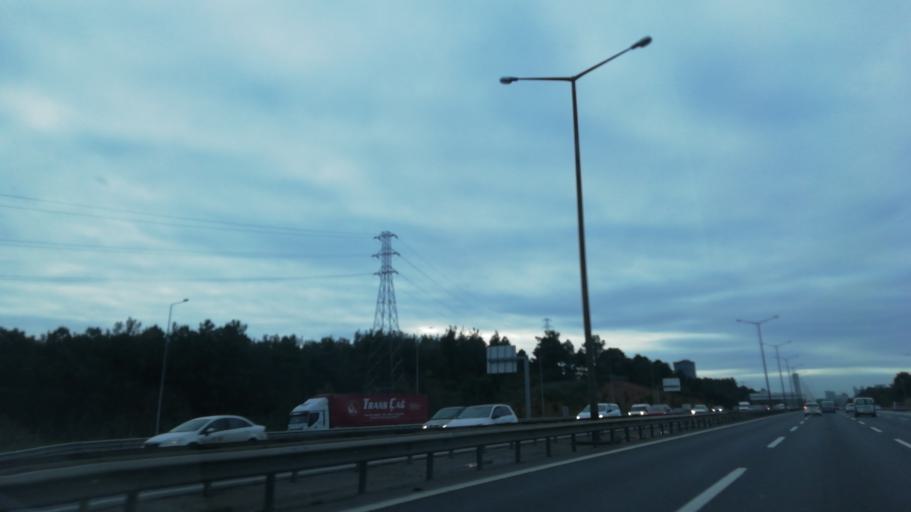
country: TR
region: Istanbul
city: Umraniye
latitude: 41.0442
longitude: 29.1212
